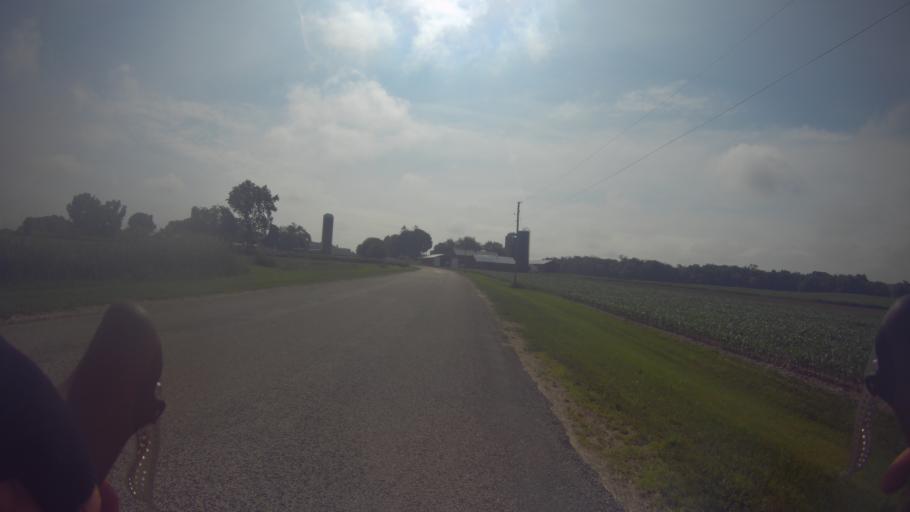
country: US
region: Wisconsin
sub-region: Dane County
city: Stoughton
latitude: 42.9797
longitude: -89.1869
